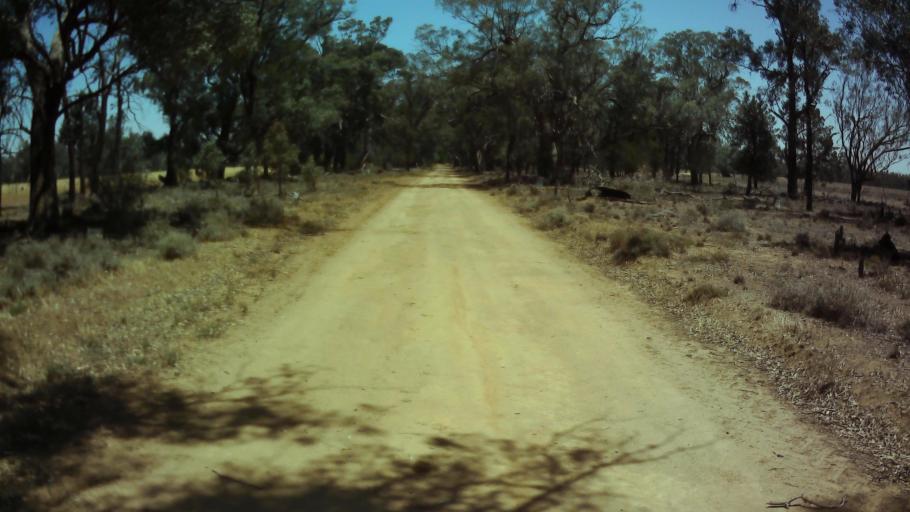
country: AU
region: New South Wales
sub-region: Weddin
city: Grenfell
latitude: -34.0437
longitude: 147.8416
